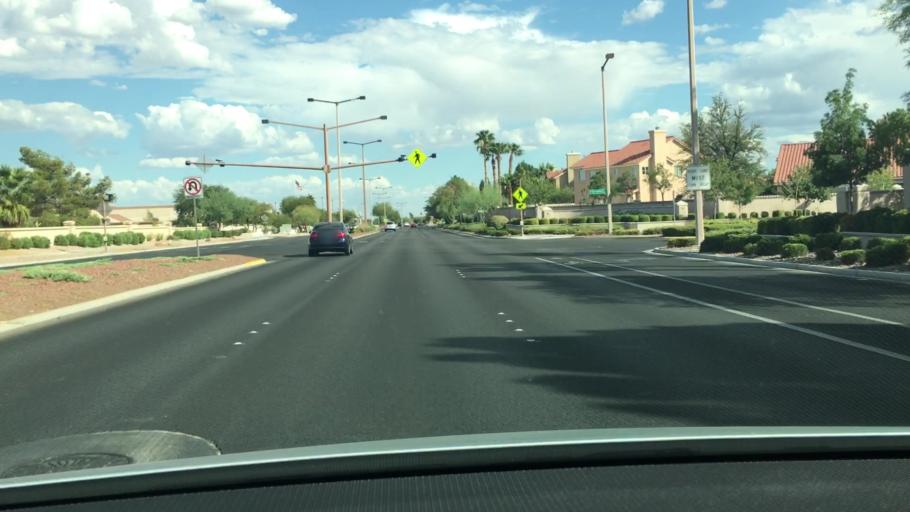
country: US
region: Nevada
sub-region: Clark County
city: Summerlin South
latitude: 36.2023
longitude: -115.2863
